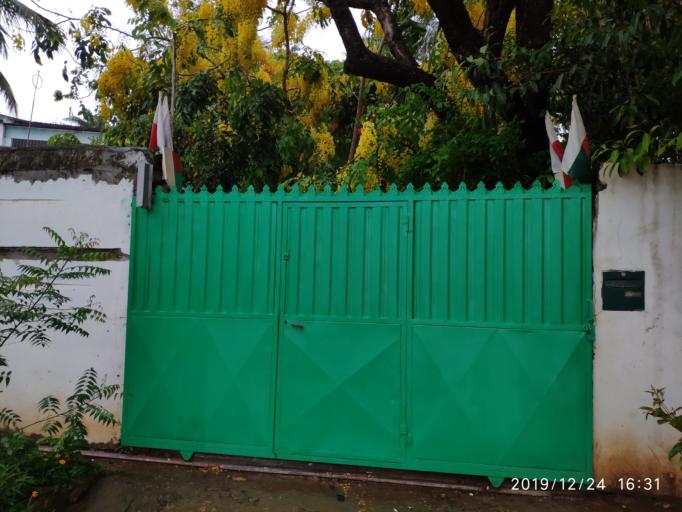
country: MG
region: Diana
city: Antsiranana
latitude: -12.2789
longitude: 49.2950
